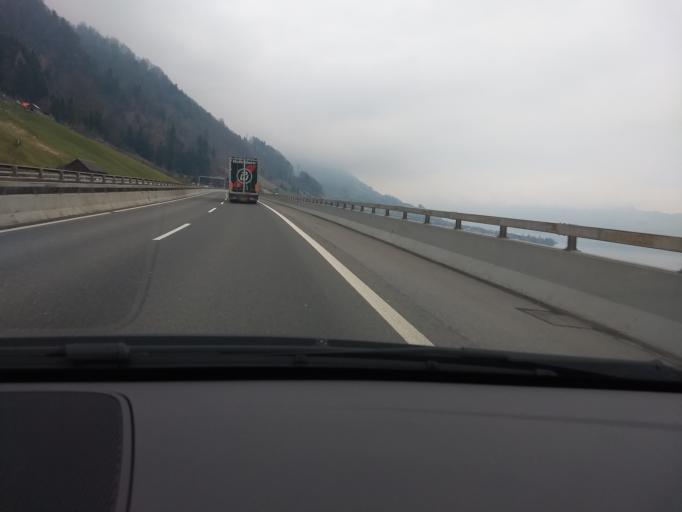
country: CH
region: Nidwalden
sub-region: Nidwalden
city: Emmetten
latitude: 46.9613
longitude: 8.4970
